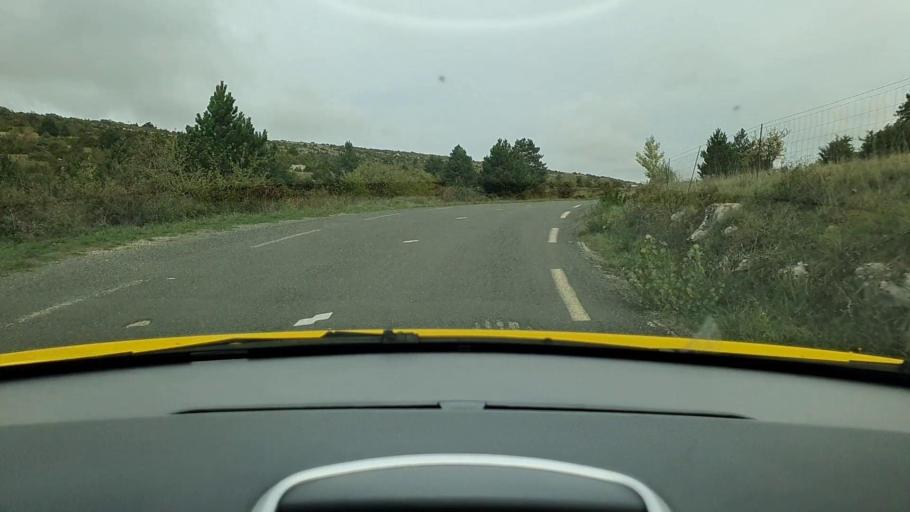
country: FR
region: Languedoc-Roussillon
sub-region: Departement de la Lozere
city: Meyrueis
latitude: 44.0924
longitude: 3.3715
